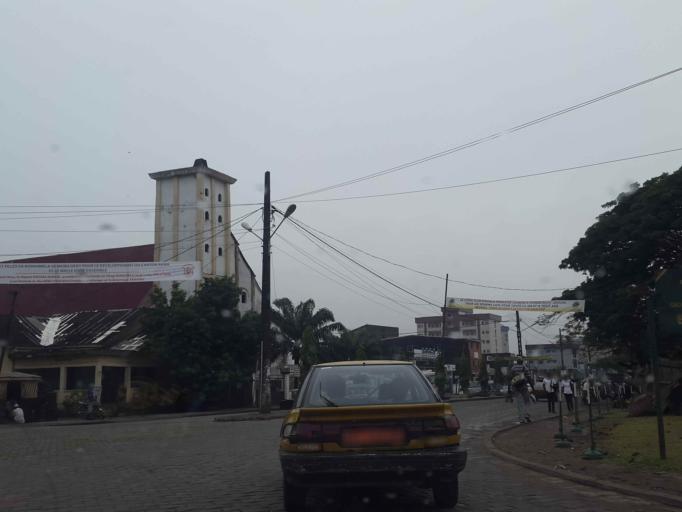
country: CM
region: Littoral
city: Douala
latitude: 4.0505
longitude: 9.7025
